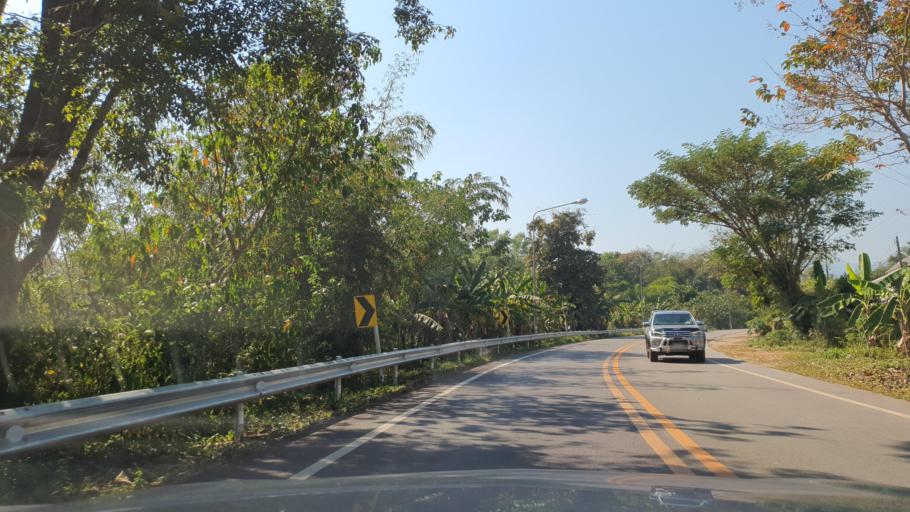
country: TH
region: Chiang Rai
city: Mae Lao
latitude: 19.8322
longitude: 99.6878
